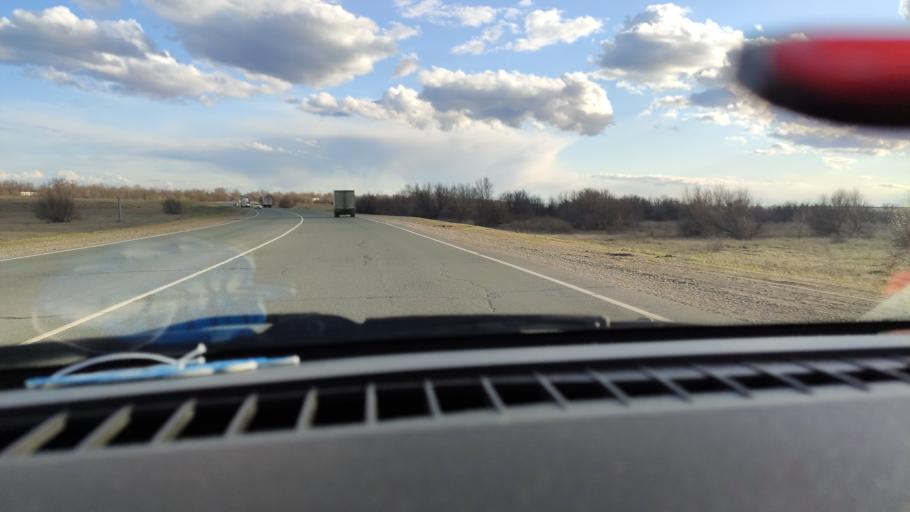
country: RU
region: Saratov
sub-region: Saratovskiy Rayon
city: Saratov
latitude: 51.7170
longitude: 46.0260
